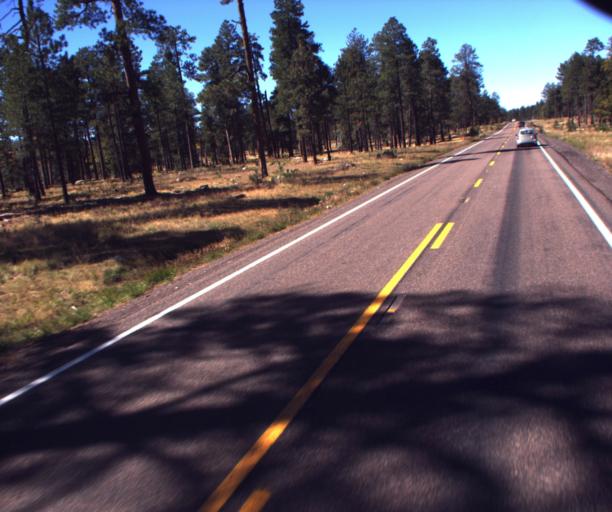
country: US
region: Arizona
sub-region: Navajo County
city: Heber-Overgaard
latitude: 34.3003
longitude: -110.8766
